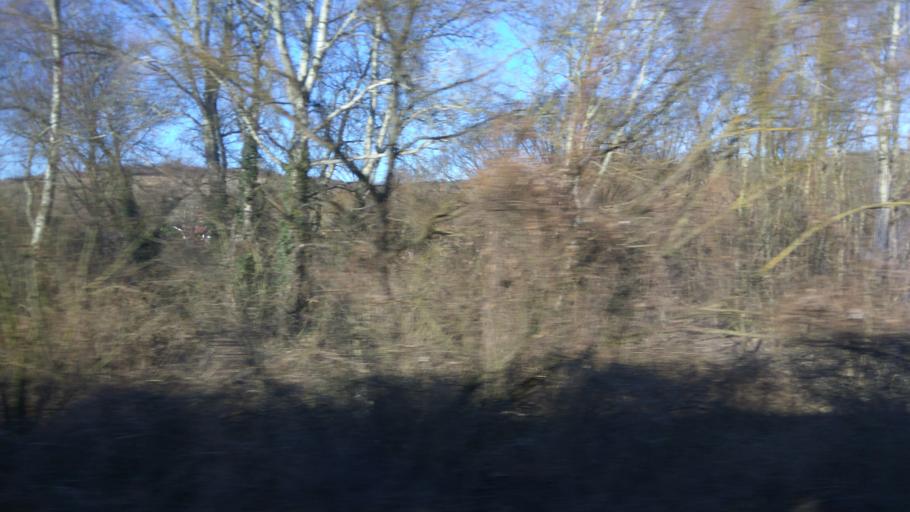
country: HU
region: Pest
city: Pecel
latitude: 47.4946
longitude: 19.3651
